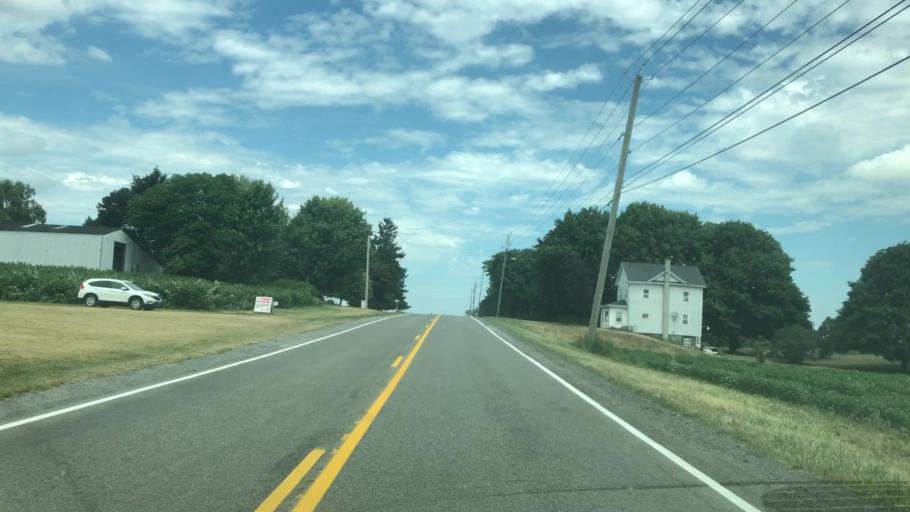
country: US
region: New York
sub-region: Monroe County
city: Webster
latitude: 43.1702
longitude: -77.4005
